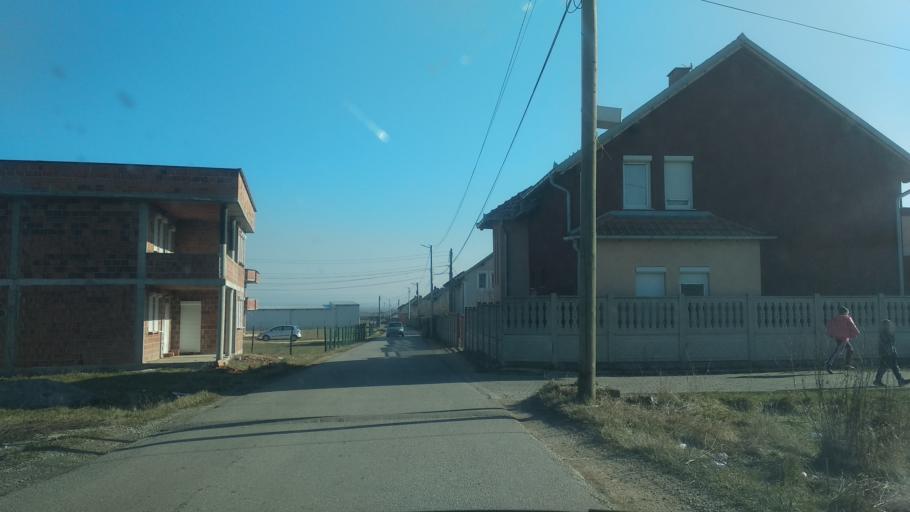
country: XK
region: Pristina
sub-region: Komuna e Gracanices
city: Glanica
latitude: 42.5830
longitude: 21.0116
